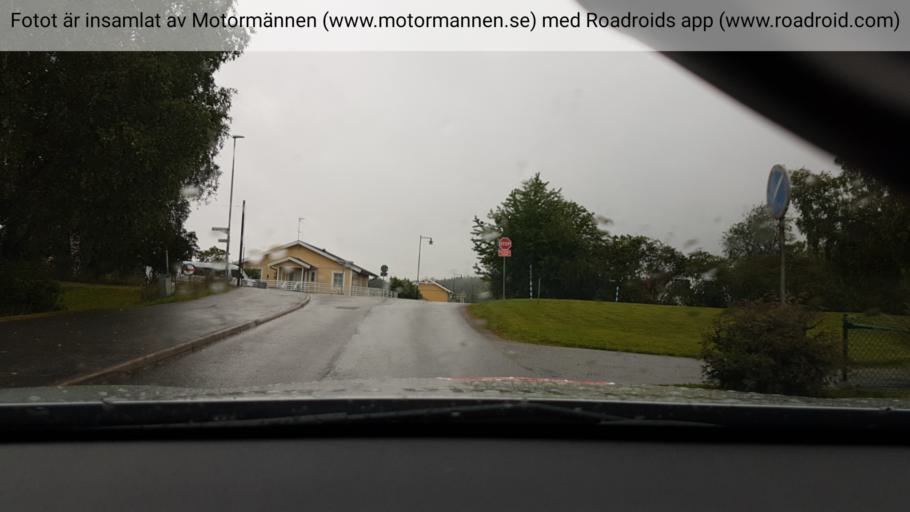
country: SE
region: Stockholm
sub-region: Haninge Kommun
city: Jordbro
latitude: 59.1054
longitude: 18.0397
